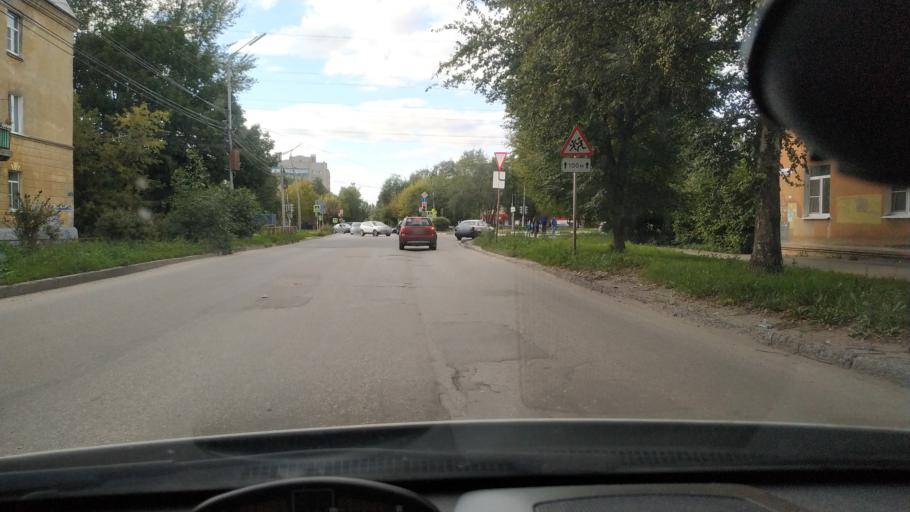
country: RU
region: Rjazan
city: Ryazan'
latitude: 54.6206
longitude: 39.7056
